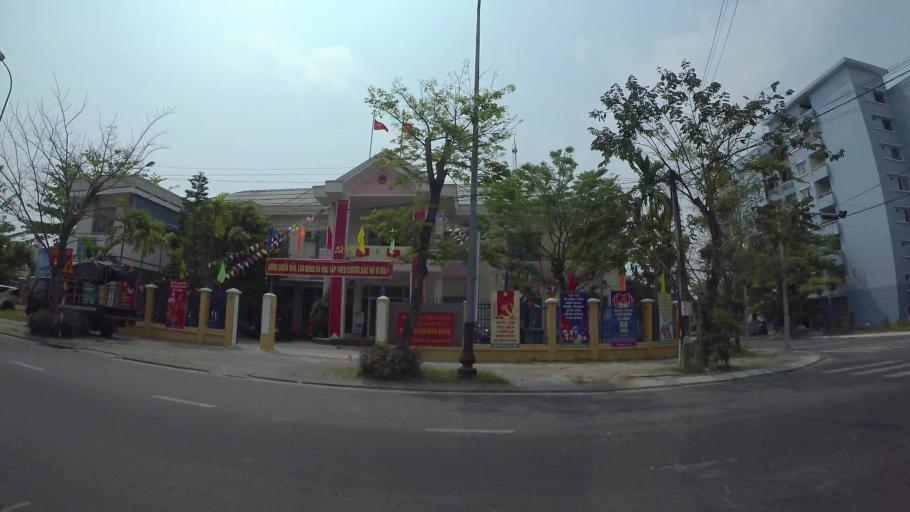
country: VN
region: Da Nang
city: Da Nang
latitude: 16.0885
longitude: 108.2311
